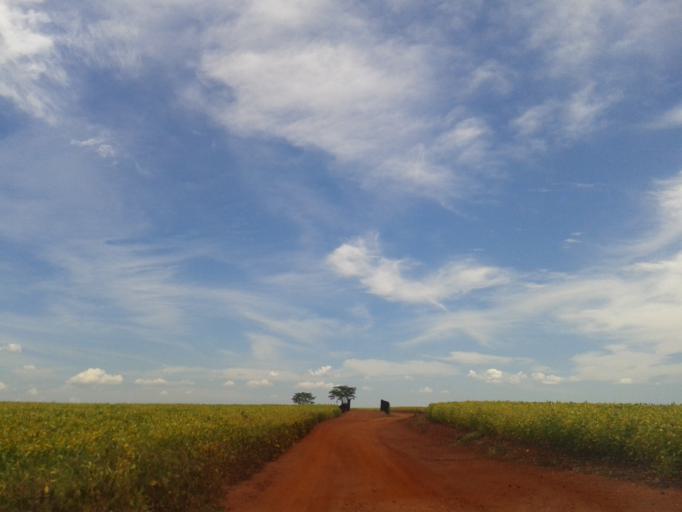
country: BR
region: Minas Gerais
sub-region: Capinopolis
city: Capinopolis
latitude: -18.6710
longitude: -49.7249
